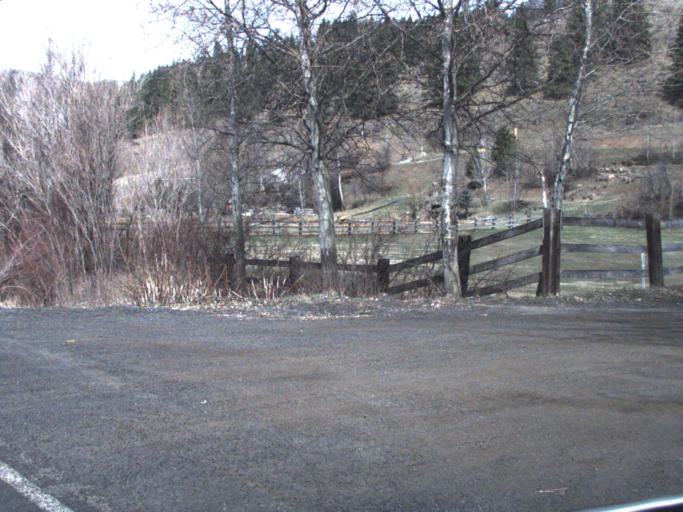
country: US
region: Washington
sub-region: Kittitas County
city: Cle Elum
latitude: 46.8979
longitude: -121.0071
